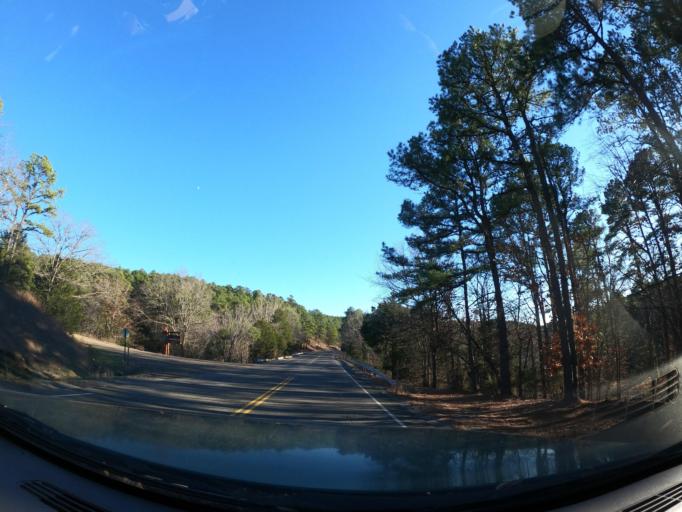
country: US
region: Oklahoma
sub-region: Latimer County
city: Wilburton
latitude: 34.9733
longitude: -95.3563
